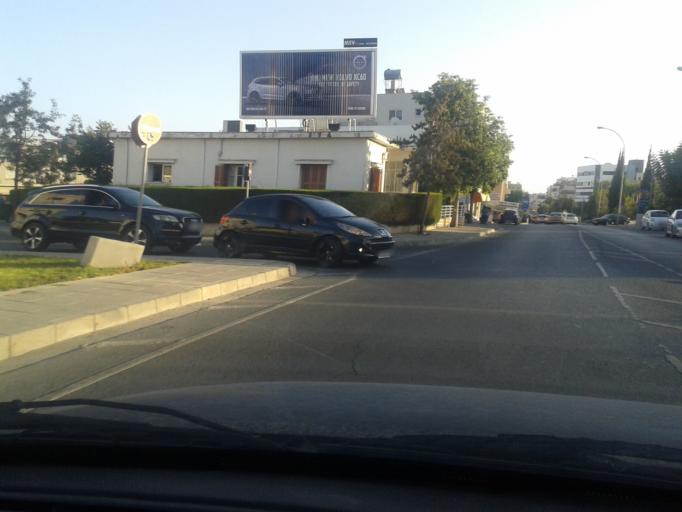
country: CY
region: Limassol
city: Limassol
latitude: 34.7003
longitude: 33.0458
